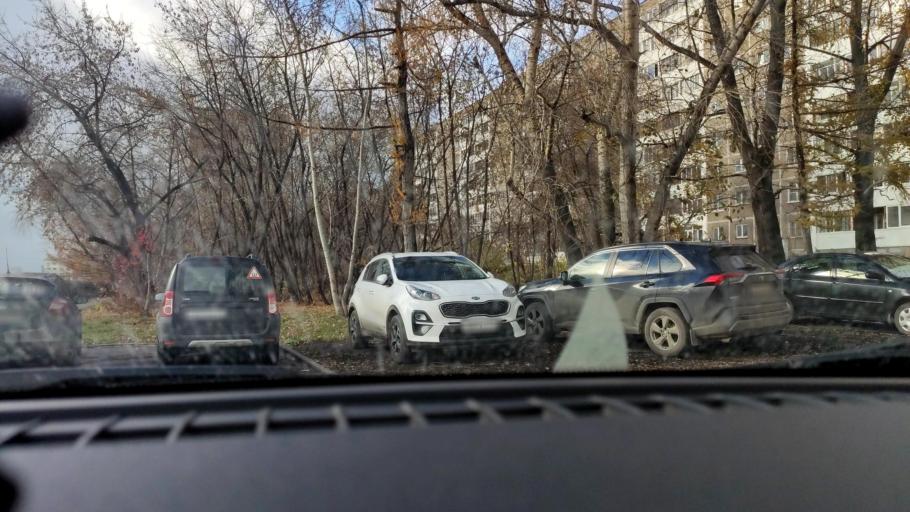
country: RU
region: Perm
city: Perm
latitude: 58.0102
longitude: 56.2182
